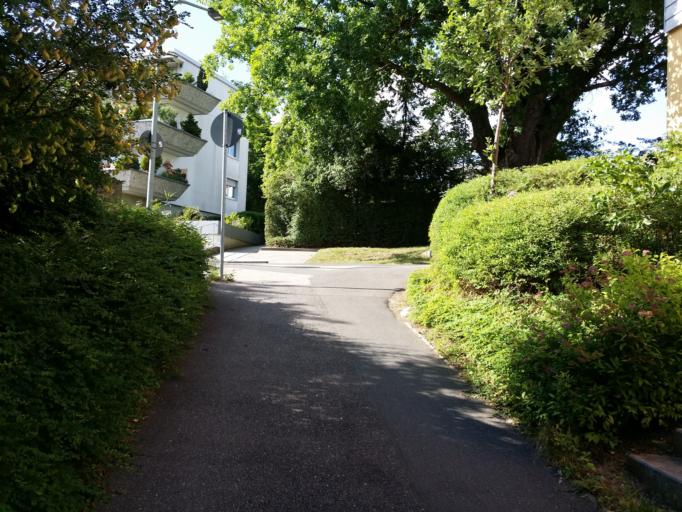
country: DE
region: Bavaria
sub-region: Upper Palatinate
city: Amberg
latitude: 49.4473
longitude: 11.8781
